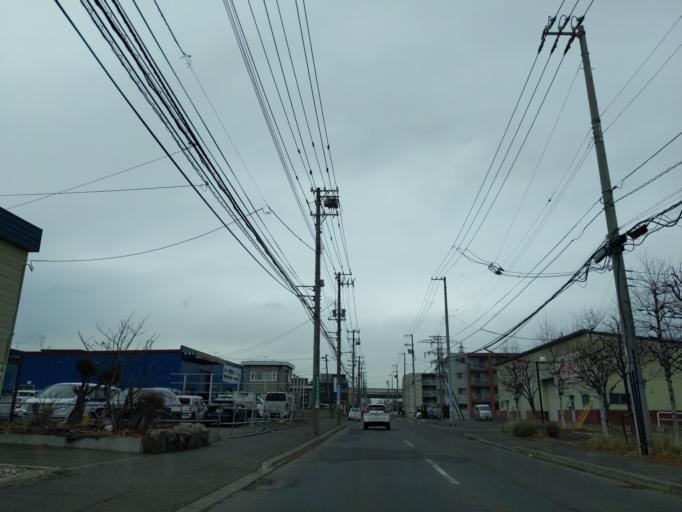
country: JP
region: Hokkaido
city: Sapporo
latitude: 43.0914
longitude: 141.4010
